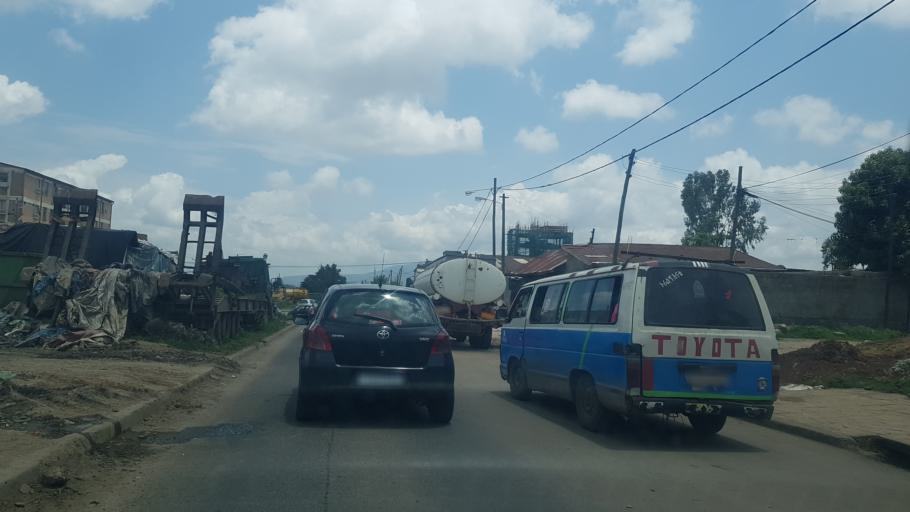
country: ET
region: Adis Abeba
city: Addis Ababa
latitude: 8.9965
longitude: 38.7541
